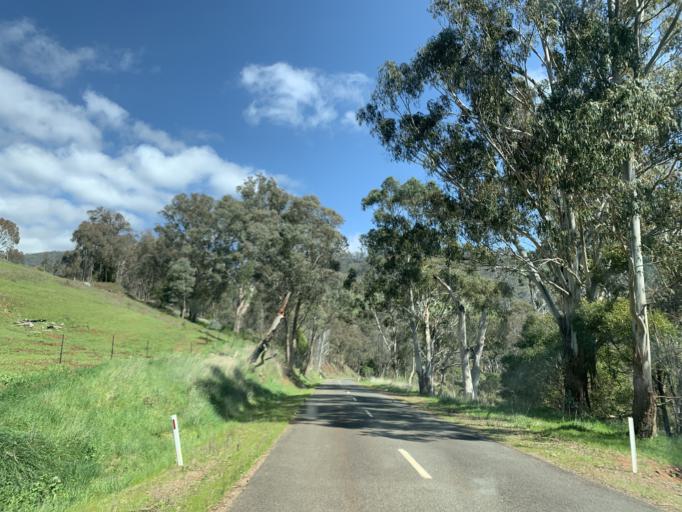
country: AU
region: Victoria
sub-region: Mansfield
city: Mansfield
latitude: -36.8277
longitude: 146.1274
